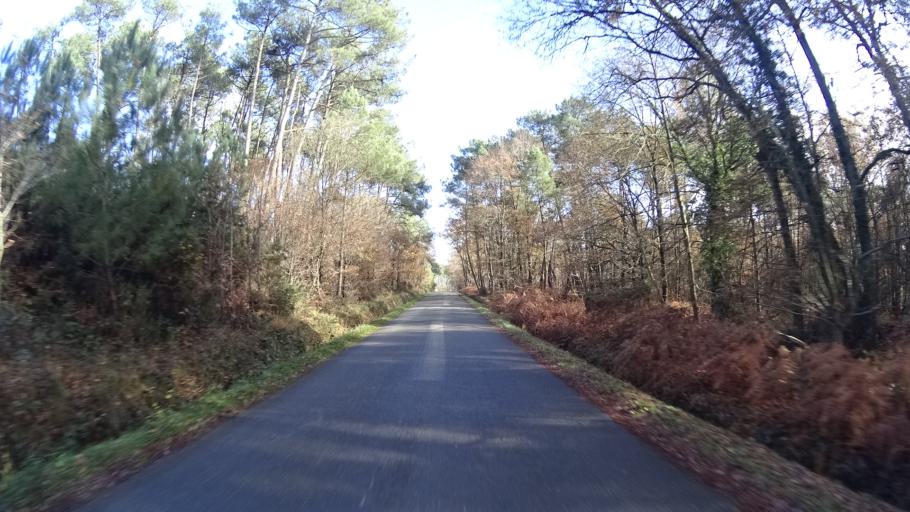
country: FR
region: Brittany
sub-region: Departement d'Ille-et-Vilaine
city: Sixt-sur-Aff
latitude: 47.8235
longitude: -2.0815
